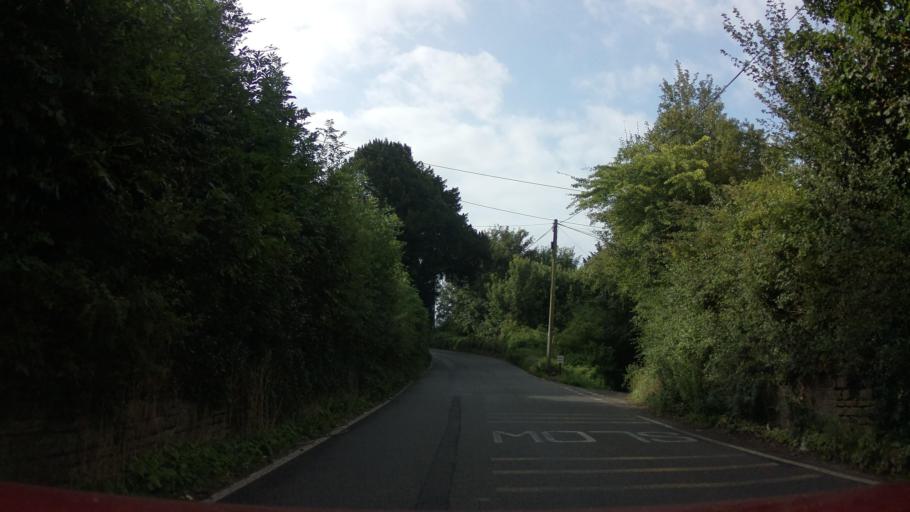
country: GB
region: England
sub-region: North Somerset
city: Nailsea
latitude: 51.4399
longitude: -2.7266
